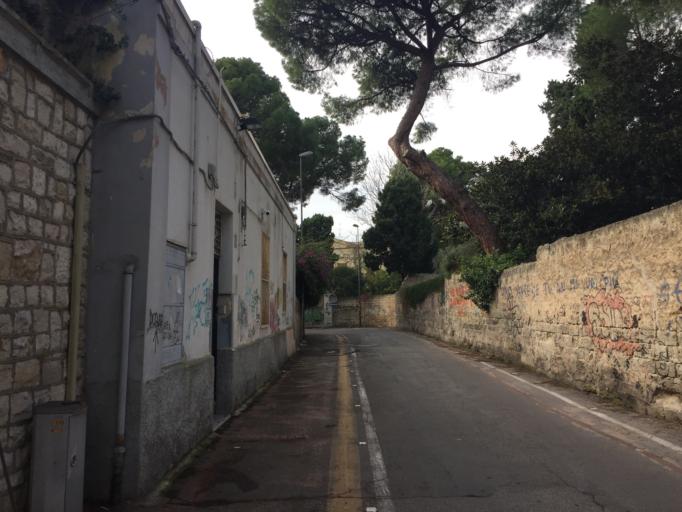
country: IT
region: Apulia
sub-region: Provincia di Bari
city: Bari
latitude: 41.1119
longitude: 16.8801
